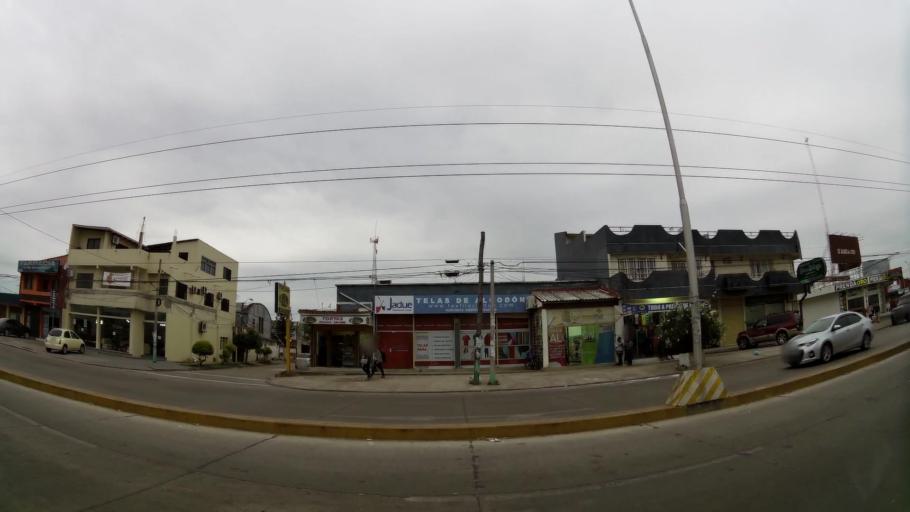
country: BO
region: Santa Cruz
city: Santa Cruz de la Sierra
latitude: -17.7783
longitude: -63.2037
